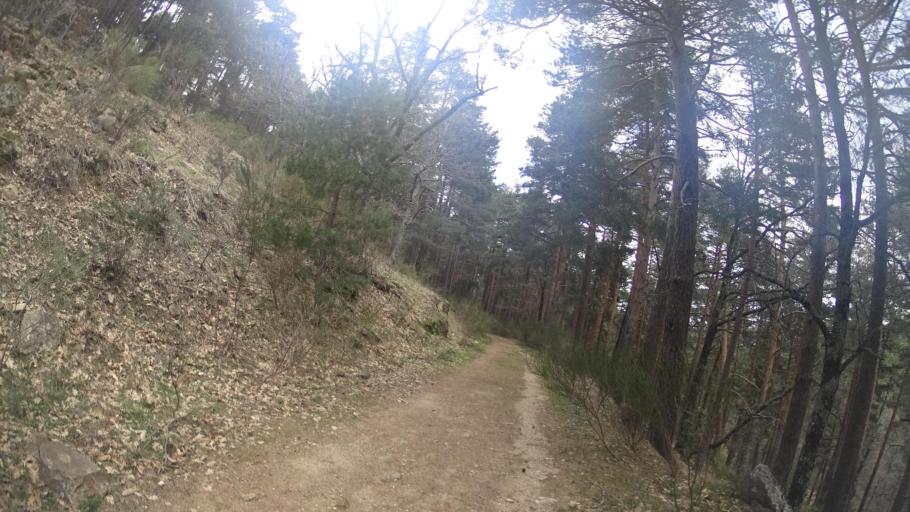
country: ES
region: Madrid
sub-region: Provincia de Madrid
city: Canencia
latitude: 40.8716
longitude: -3.7830
